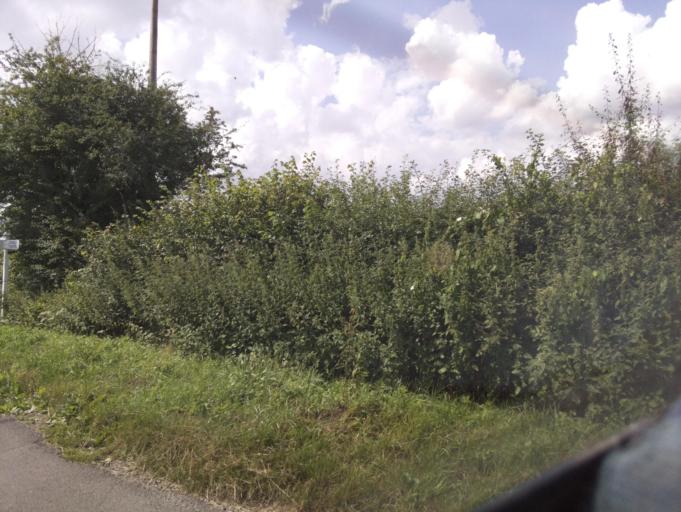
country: GB
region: England
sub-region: Wiltshire
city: Hankerton
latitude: 51.6150
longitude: -2.0451
